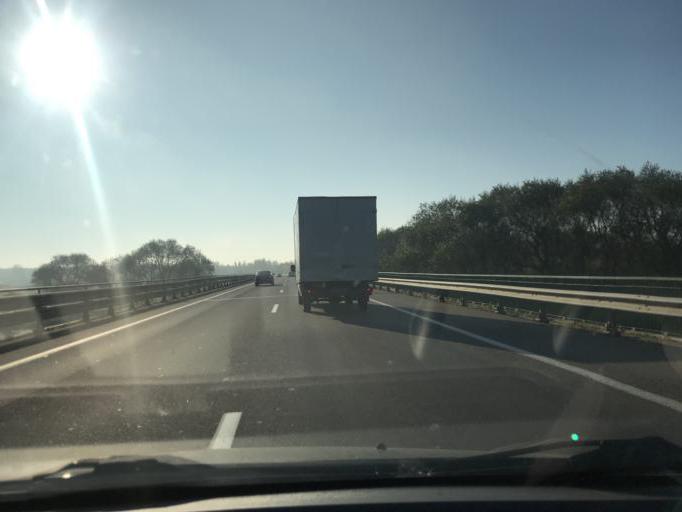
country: BY
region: Minsk
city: Dukora
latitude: 53.6649
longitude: 27.9388
